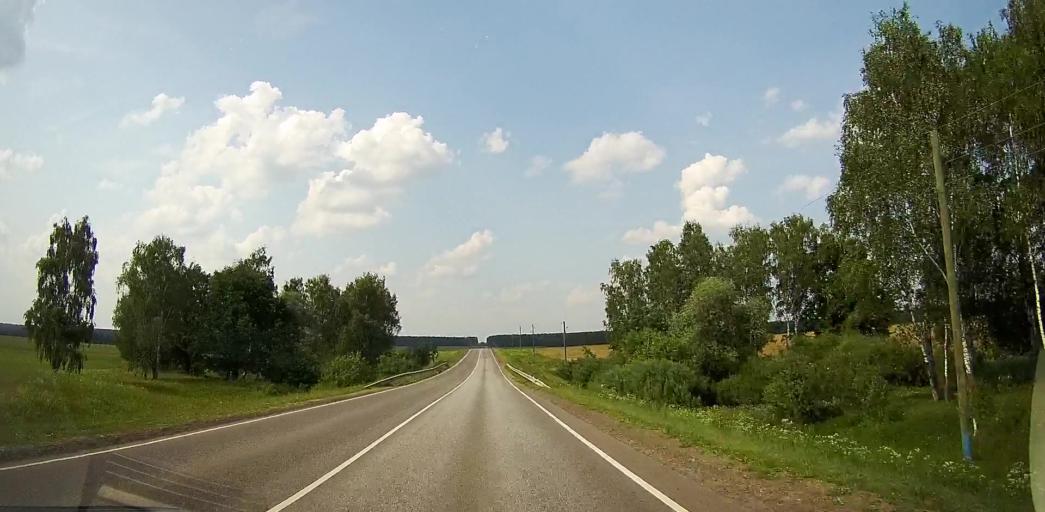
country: RU
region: Moskovskaya
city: Malino
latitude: 55.0413
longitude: 38.1526
